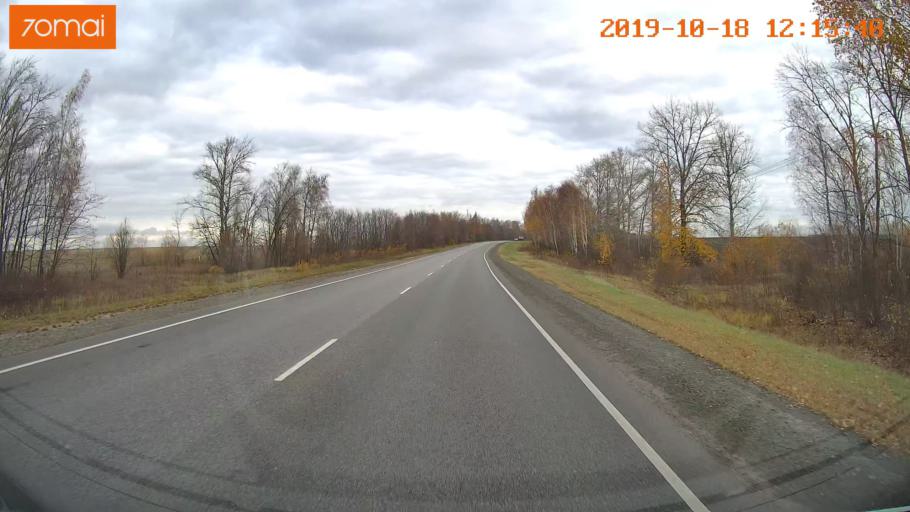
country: RU
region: Rjazan
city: Zakharovo
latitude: 54.4469
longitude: 39.4040
